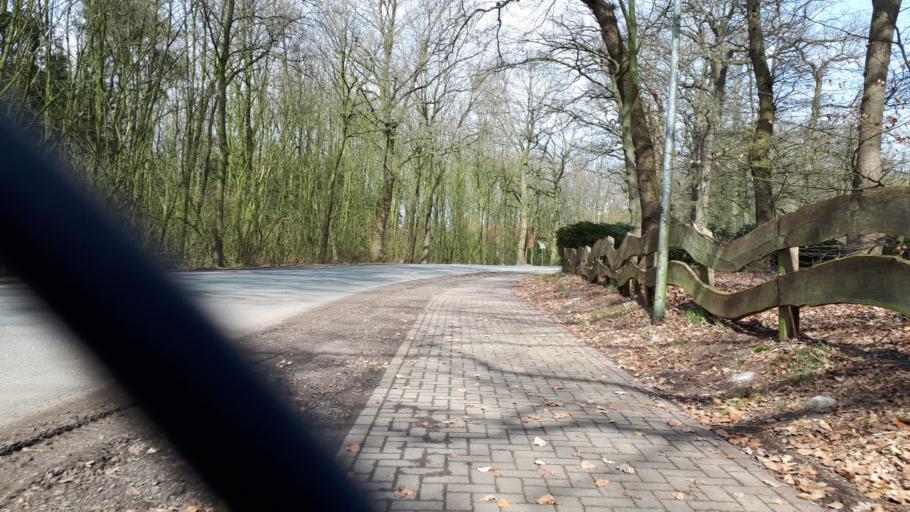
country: DE
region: Lower Saxony
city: Cloppenburg
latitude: 52.8538
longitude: 7.9941
